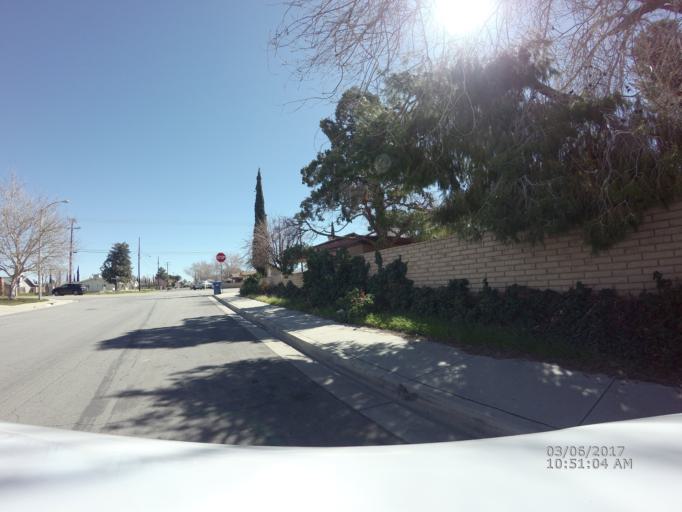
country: US
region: California
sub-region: Los Angeles County
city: Quartz Hill
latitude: 34.6547
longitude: -118.2280
